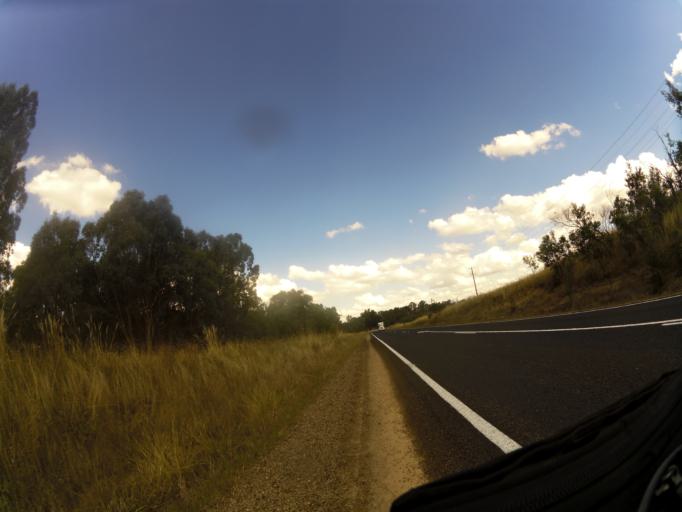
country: AU
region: Victoria
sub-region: Mansfield
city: Mansfield
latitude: -36.9080
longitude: 145.9984
